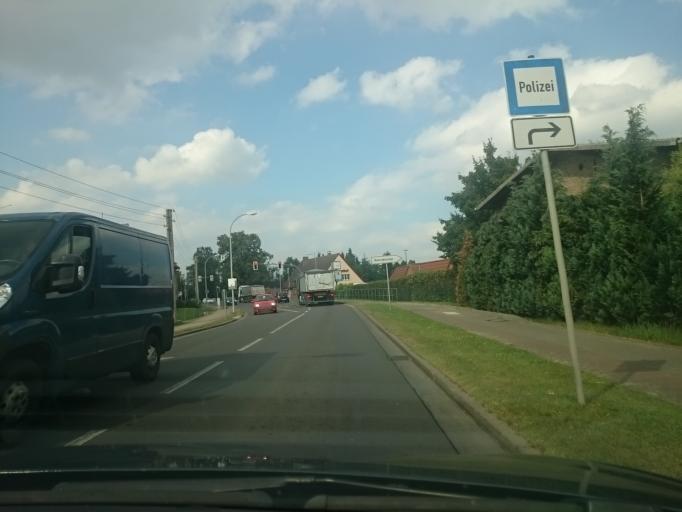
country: DE
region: Mecklenburg-Vorpommern
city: Ducherow
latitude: 53.7637
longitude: 13.7785
